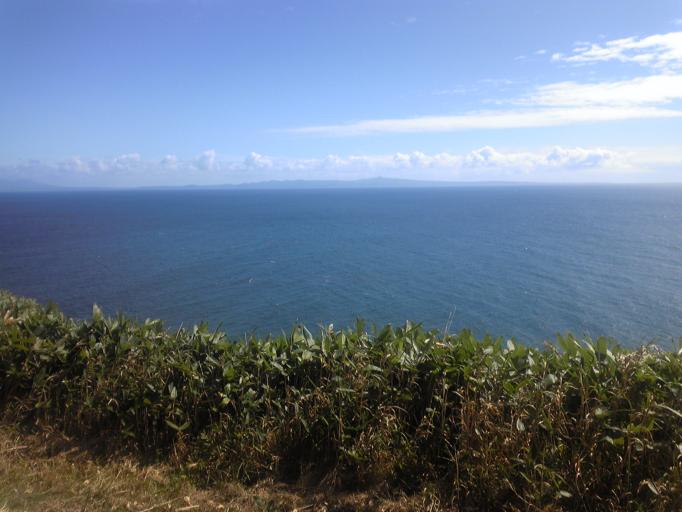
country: JP
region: Hokkaido
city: Shibetsu
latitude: 44.0374
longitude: 145.2199
